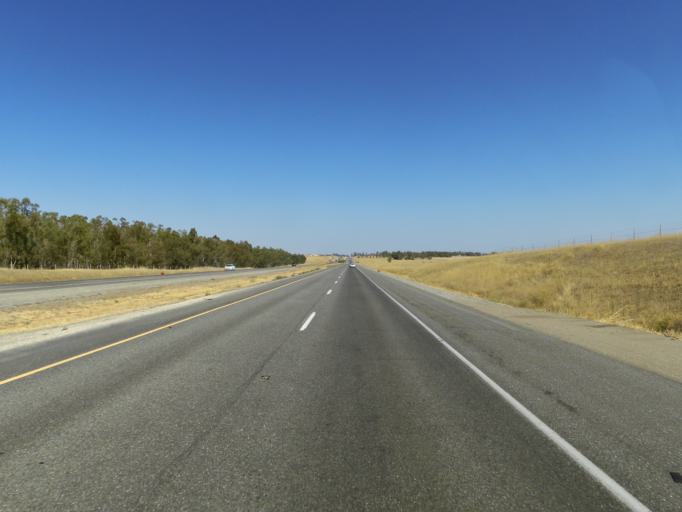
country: US
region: California
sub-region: Tehama County
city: Corning
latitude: 39.8490
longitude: -122.1999
